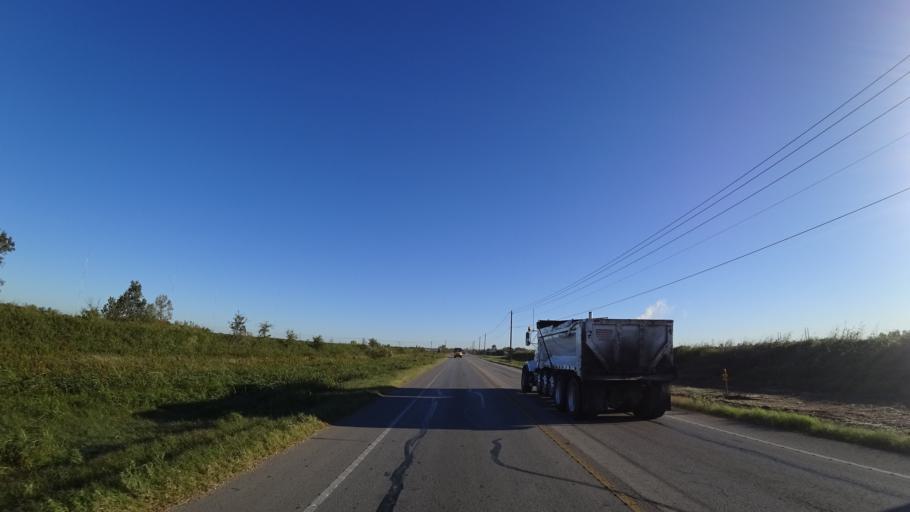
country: US
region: Texas
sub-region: Travis County
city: Hornsby Bend
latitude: 30.2309
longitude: -97.6284
